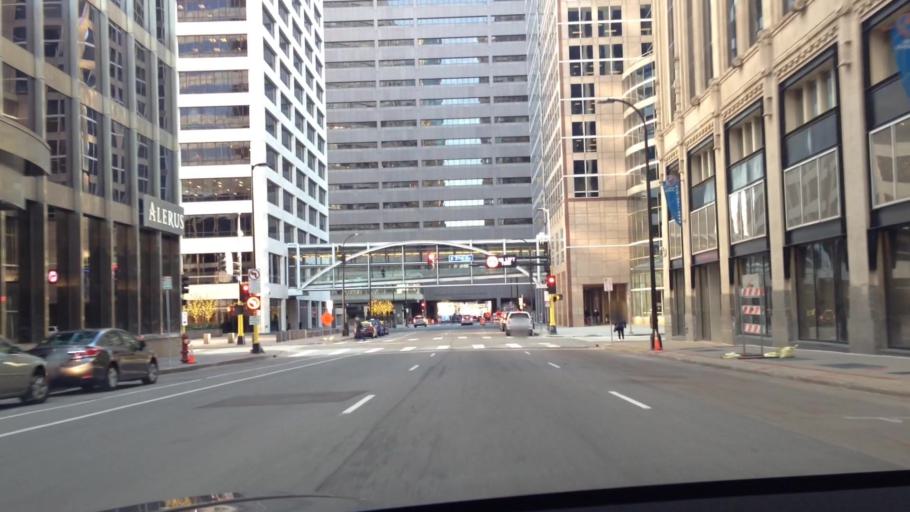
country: US
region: Minnesota
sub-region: Hennepin County
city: Minneapolis
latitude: 44.9770
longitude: -93.2695
